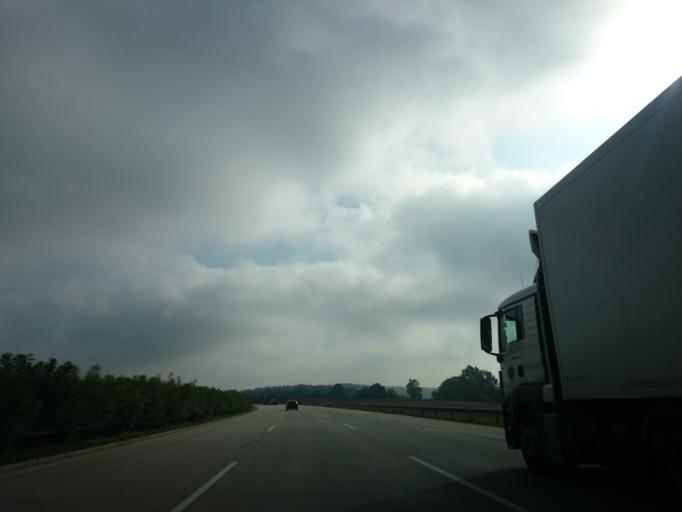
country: CZ
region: Olomoucky
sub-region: Okres Prerov
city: Hranice
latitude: 49.5770
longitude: 17.7404
